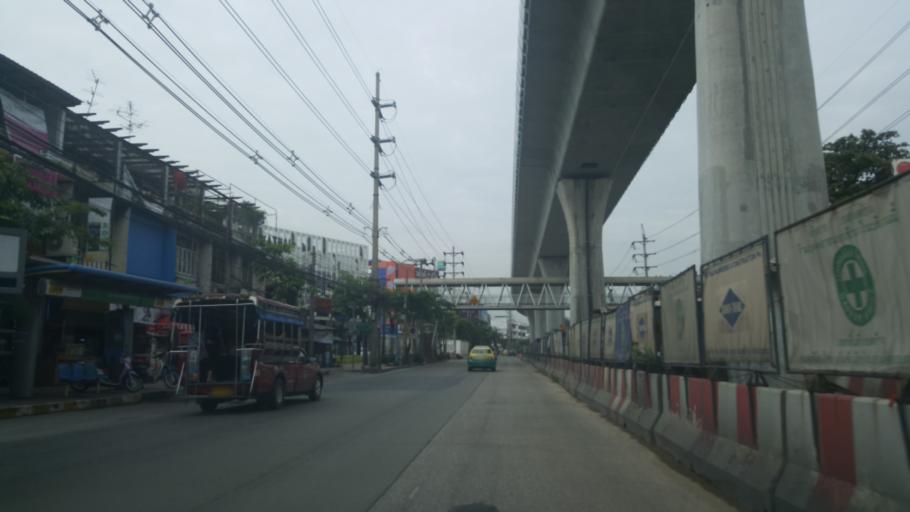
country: TH
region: Bangkok
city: Phasi Charoen
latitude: 13.7187
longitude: 100.4544
